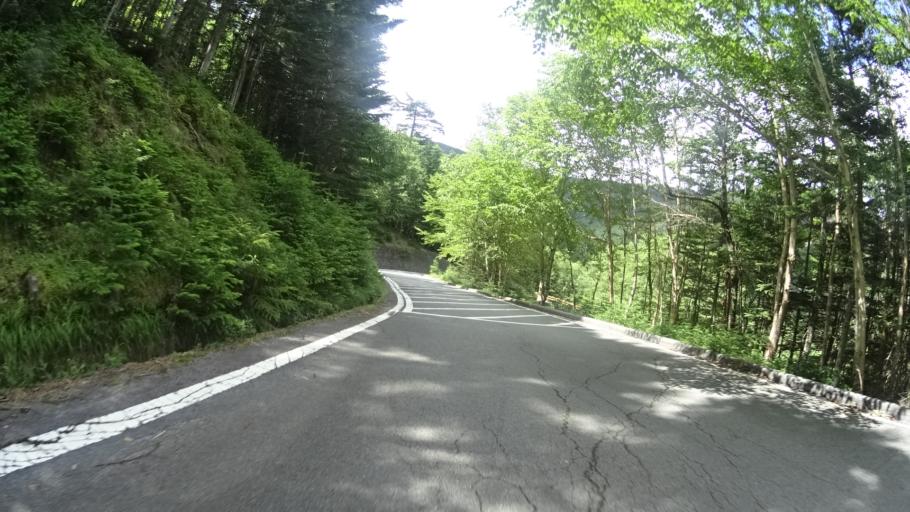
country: JP
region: Yamanashi
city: Enzan
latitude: 35.8661
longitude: 138.6607
